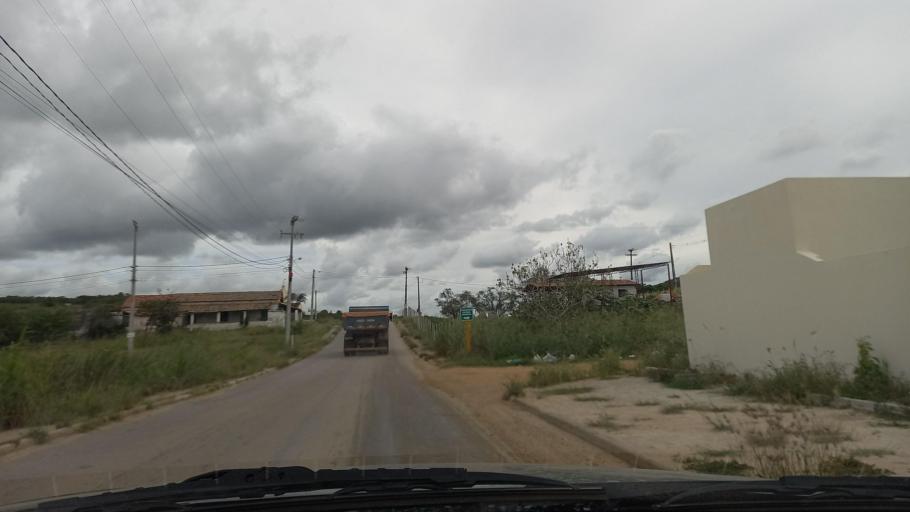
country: BR
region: Pernambuco
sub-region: Gravata
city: Gravata
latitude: -8.2243
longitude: -35.5793
